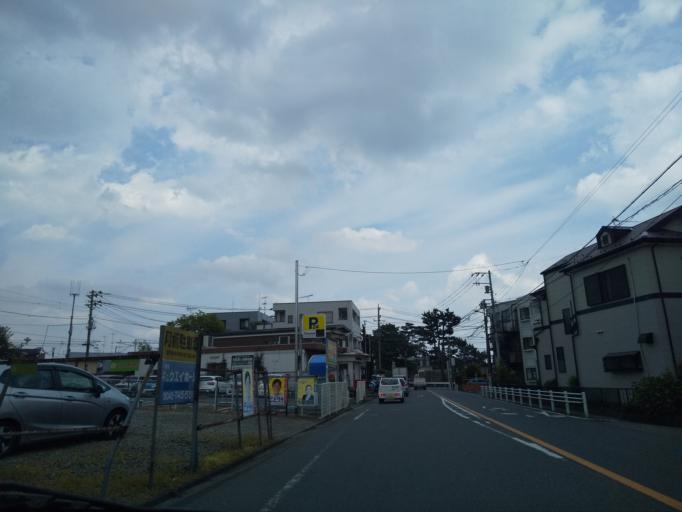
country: JP
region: Kanagawa
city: Zama
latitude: 35.5241
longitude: 139.4109
